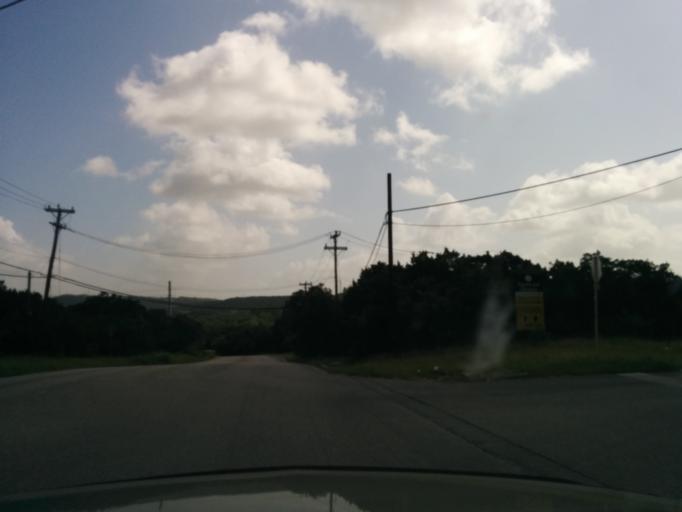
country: US
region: Texas
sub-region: Bexar County
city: Cross Mountain
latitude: 29.5973
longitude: -98.6302
